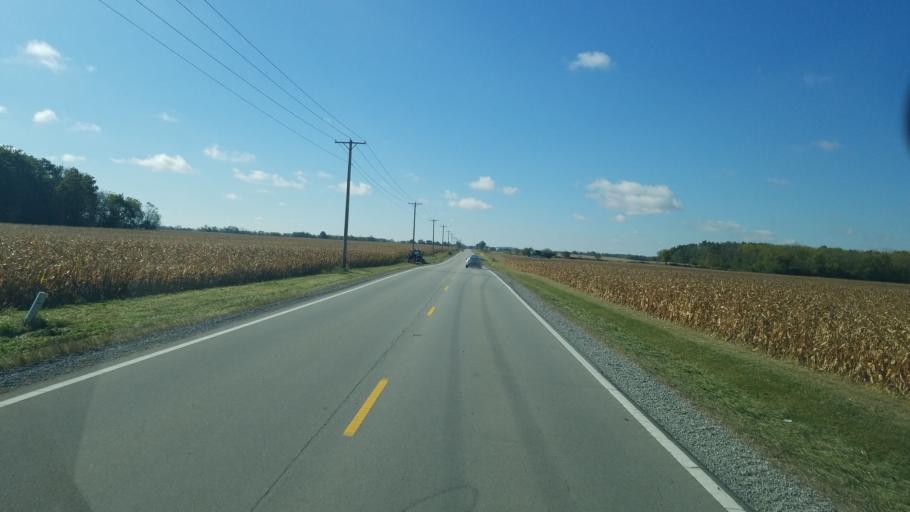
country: US
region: Ohio
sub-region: Highland County
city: Leesburg
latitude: 39.4182
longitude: -83.5213
